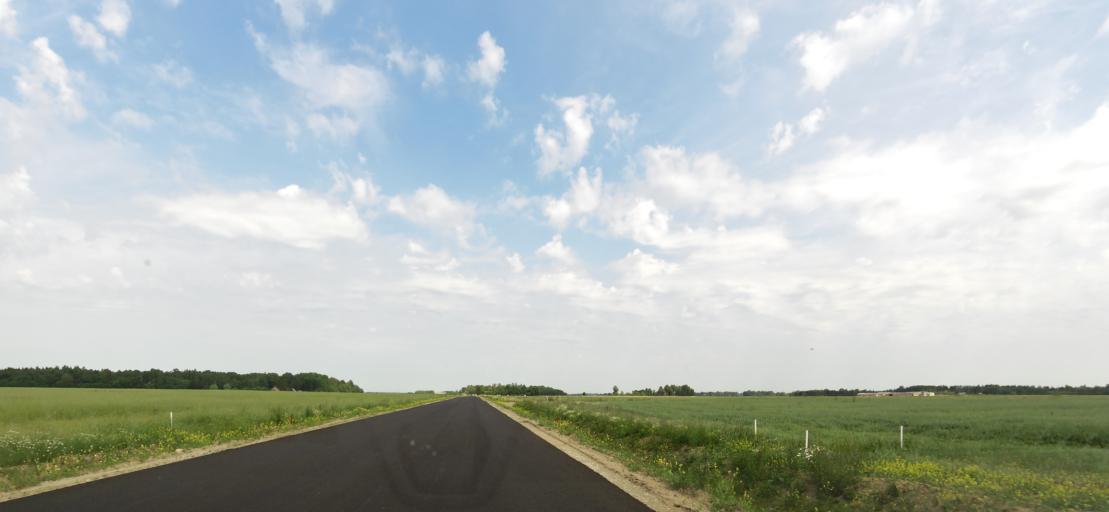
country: LT
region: Panevezys
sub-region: Birzai
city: Birzai
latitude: 56.2902
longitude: 24.6070
